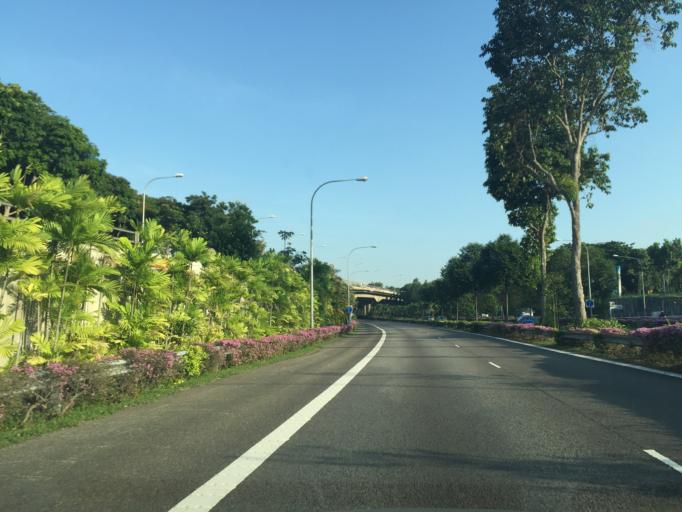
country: SG
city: Singapore
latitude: 1.3473
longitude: 103.9667
